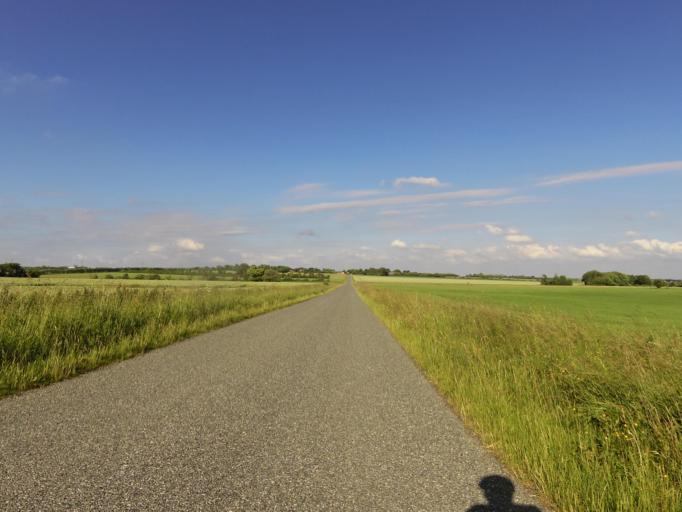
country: DK
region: South Denmark
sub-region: Vejen Kommune
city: Rodding
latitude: 55.3435
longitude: 9.1107
